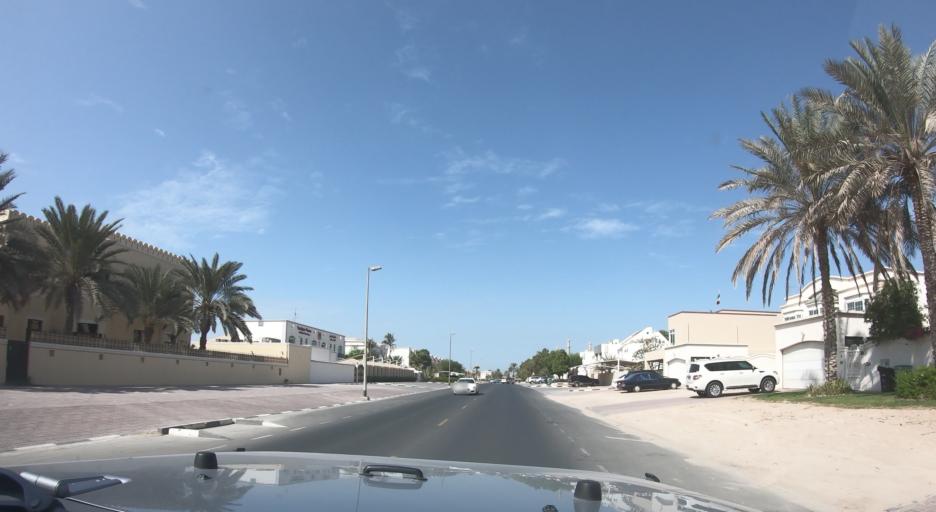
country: AE
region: Dubai
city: Dubai
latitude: 25.1603
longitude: 55.2243
